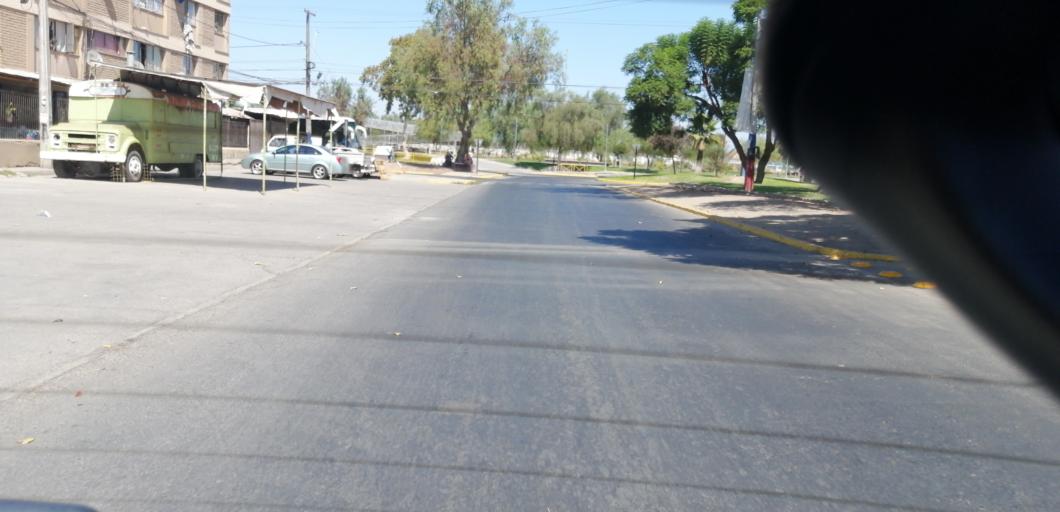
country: CL
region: Santiago Metropolitan
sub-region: Provincia de Santiago
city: Lo Prado
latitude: -33.4491
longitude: -70.7544
